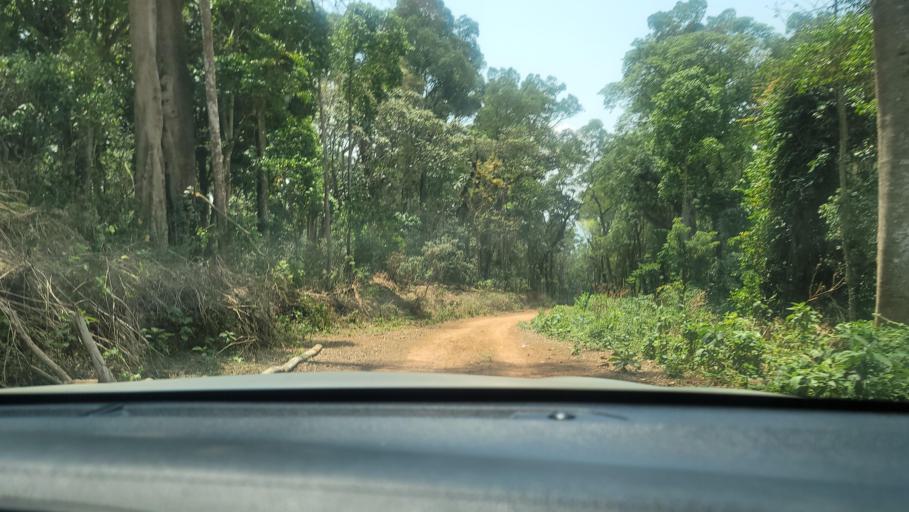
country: ET
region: Southern Nations, Nationalities, and People's Region
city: Bonga
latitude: 7.5424
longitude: 36.1802
